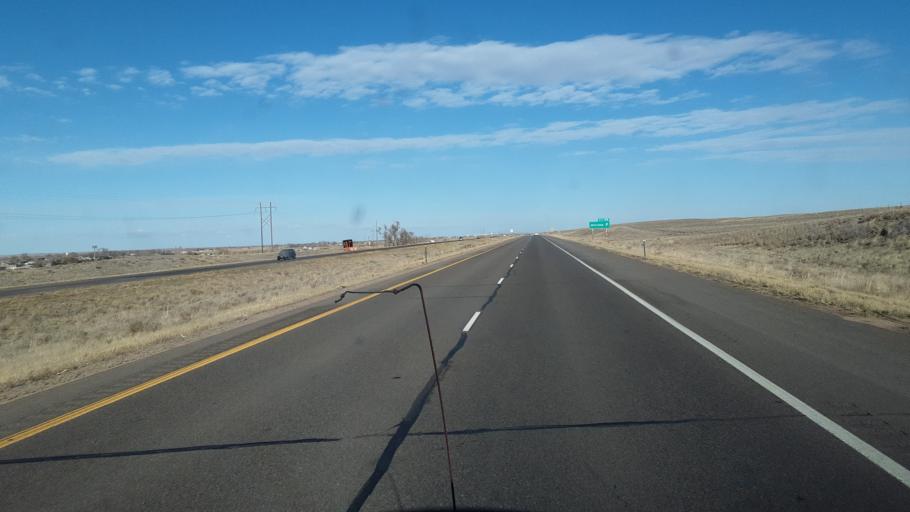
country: US
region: Colorado
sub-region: Morgan County
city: Brush
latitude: 40.2966
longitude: -103.5354
